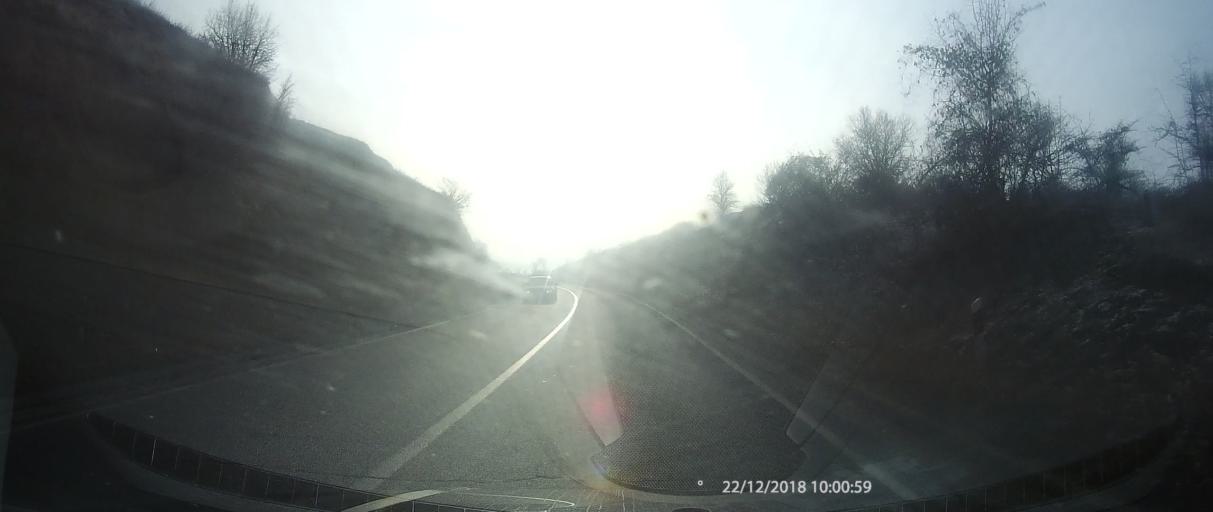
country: MK
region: Opstina Rankovce
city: Rankovce
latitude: 42.1463
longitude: 21.9887
